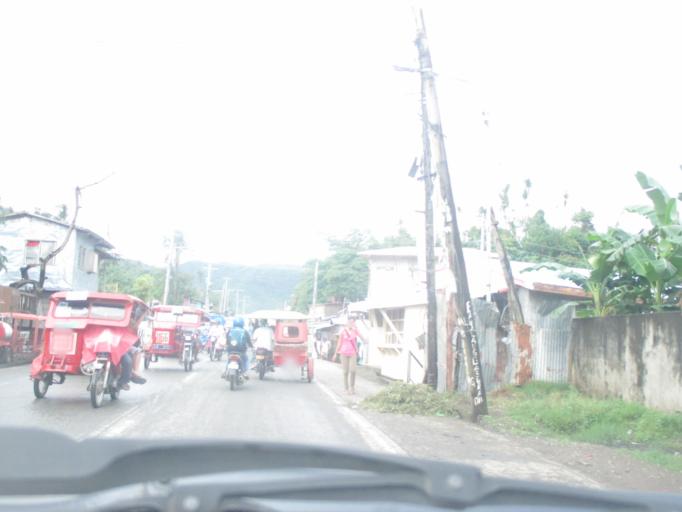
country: PH
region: Eastern Visayas
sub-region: Province of Leyte
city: Panalanoy
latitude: 11.2466
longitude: 124.9956
